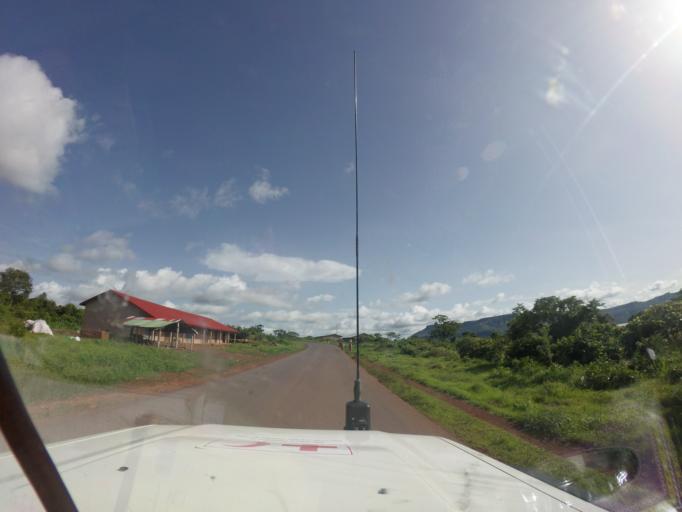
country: GN
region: Mamou
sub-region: Mamou Prefecture
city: Mamou
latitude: 10.2665
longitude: -12.4531
